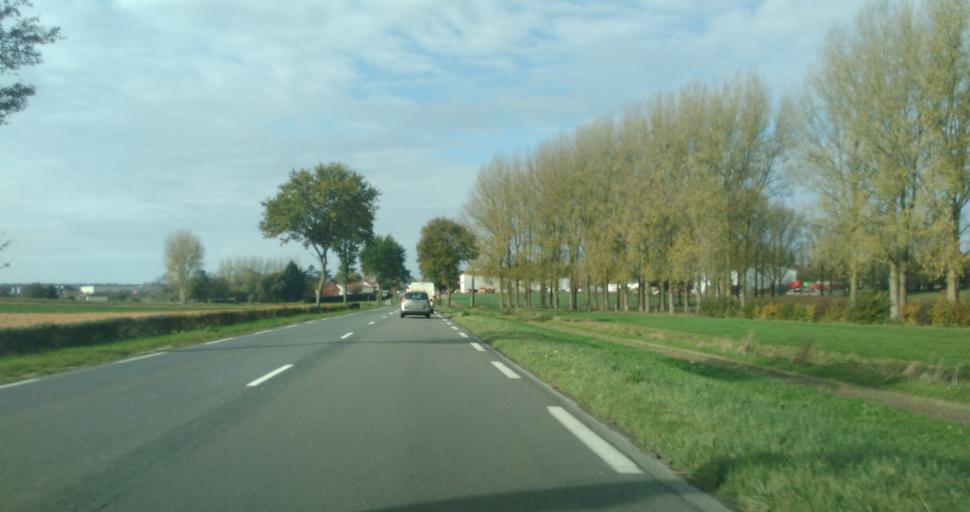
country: FR
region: Nord-Pas-de-Calais
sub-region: Departement du Pas-de-Calais
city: Savy-Berlette
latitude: 50.3529
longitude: 2.4998
